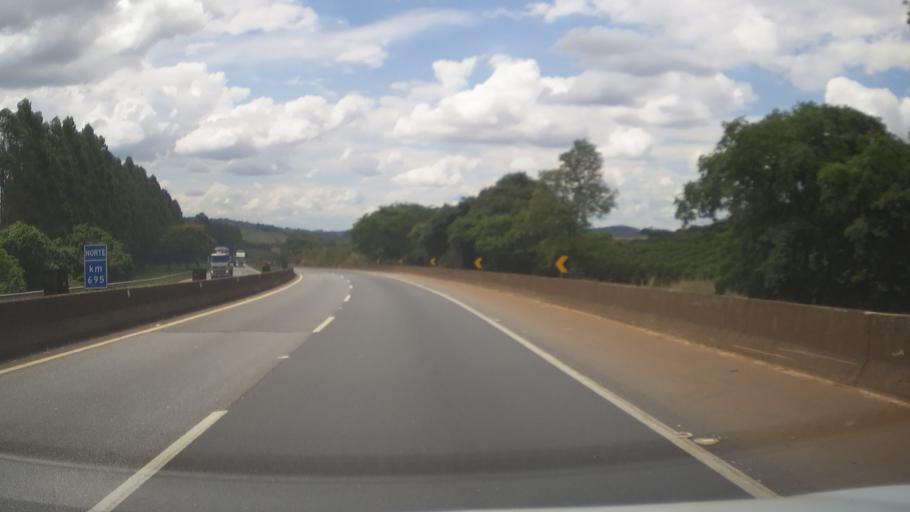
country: BR
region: Minas Gerais
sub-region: Nepomuceno
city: Nepomuceno
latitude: -21.2422
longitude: -45.1356
